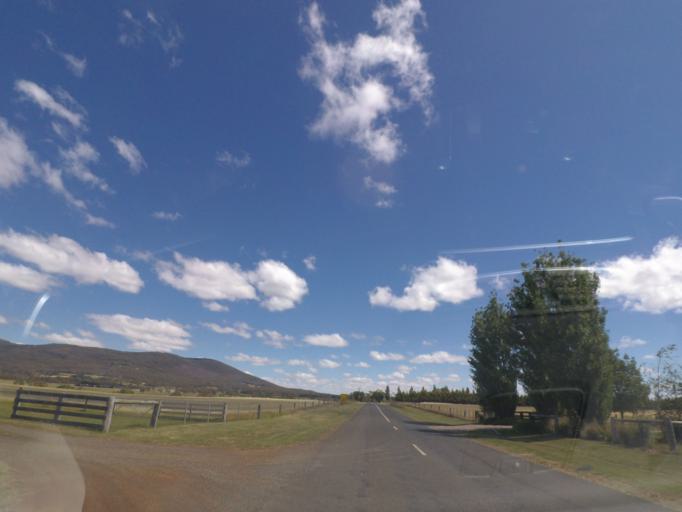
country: AU
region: Victoria
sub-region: Hume
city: Sunbury
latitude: -37.3359
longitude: 144.5581
